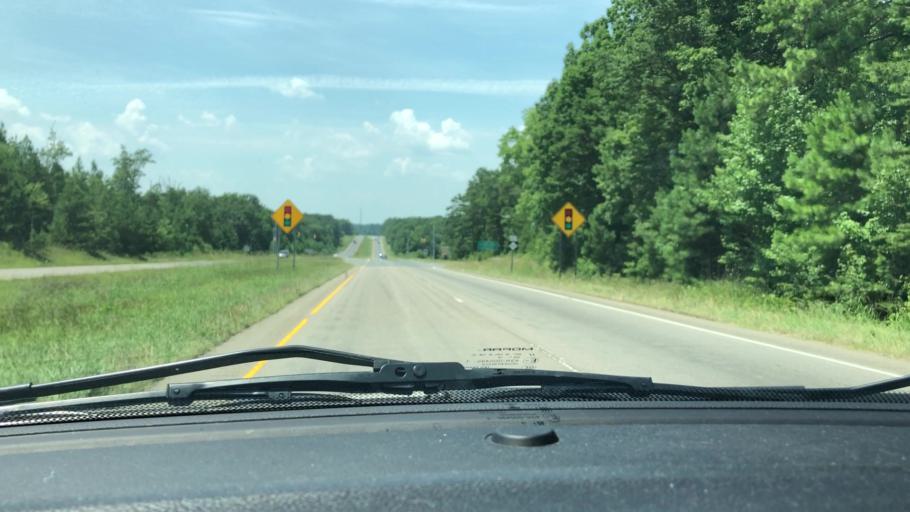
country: US
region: North Carolina
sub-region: Chatham County
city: Siler City
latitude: 35.6293
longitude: -79.3665
